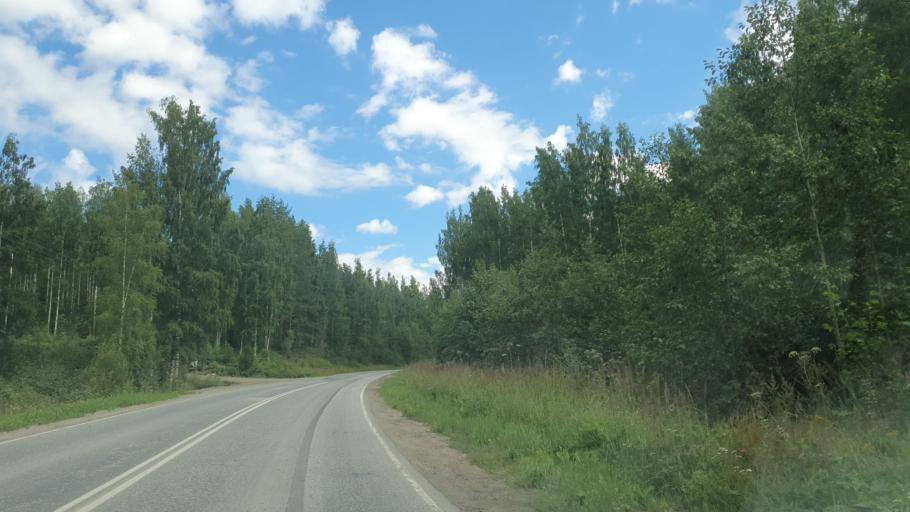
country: FI
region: Central Finland
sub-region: Jyvaeskylae
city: Muurame
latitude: 62.1455
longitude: 25.7148
